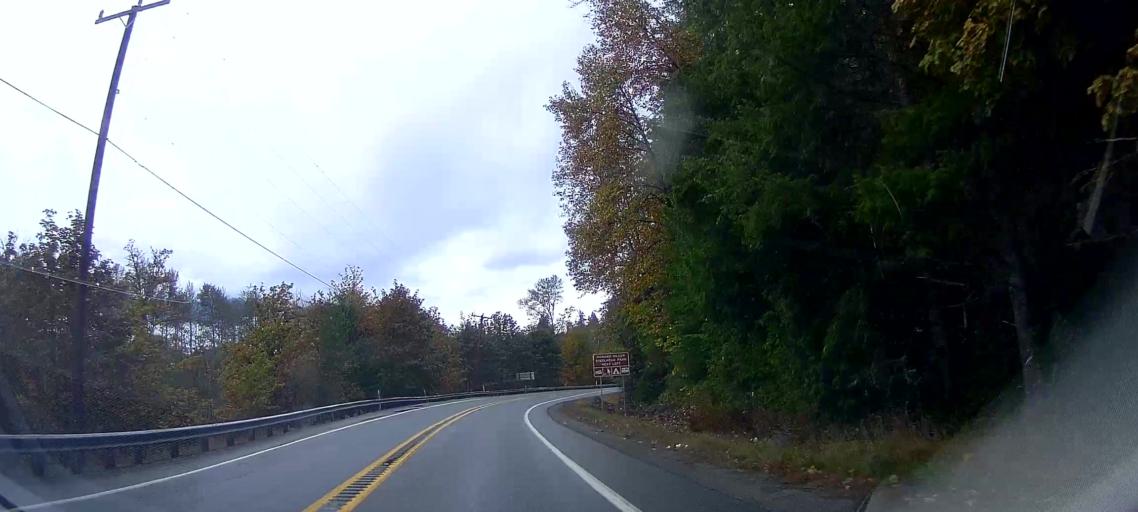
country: US
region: Washington
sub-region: Snohomish County
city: Darrington
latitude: 48.4884
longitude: -121.5859
